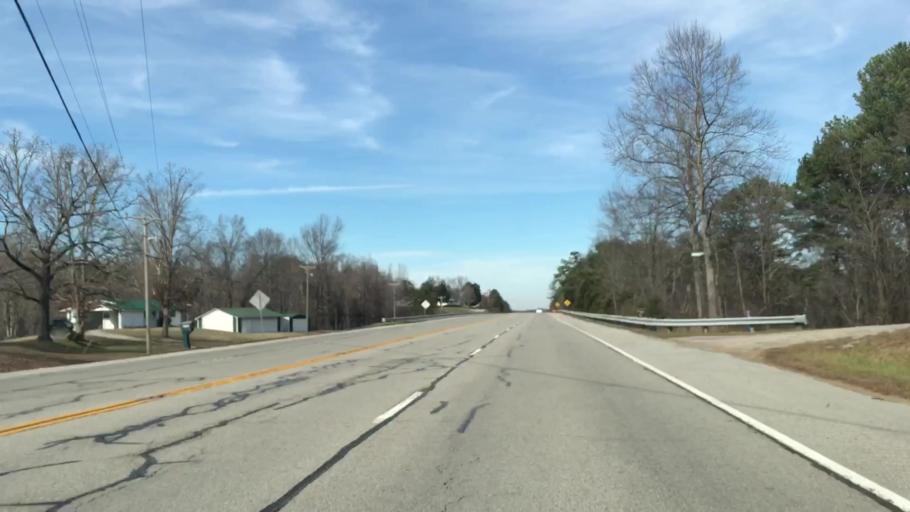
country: US
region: Kentucky
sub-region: Pulaski County
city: Somerset
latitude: 36.9225
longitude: -84.5192
